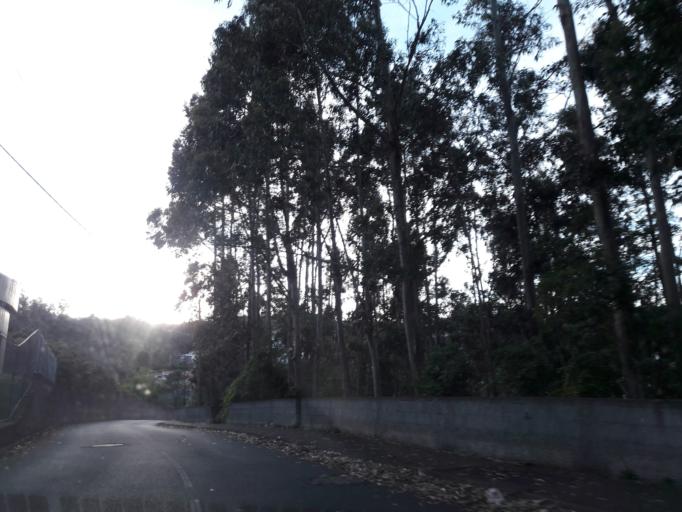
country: PT
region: Madeira
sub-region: Santa Cruz
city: Camacha
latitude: 32.6848
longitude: -16.8503
